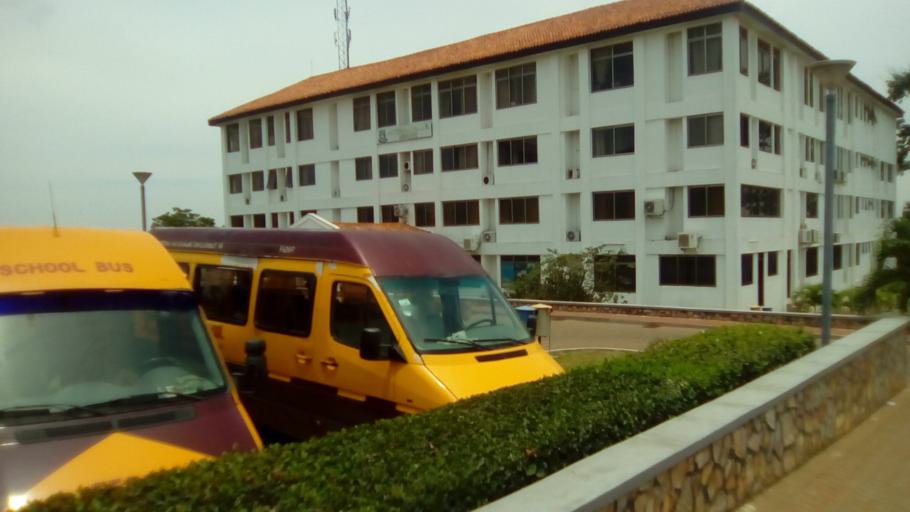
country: GH
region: Greater Accra
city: Medina Estates
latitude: 5.6534
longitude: -0.1824
